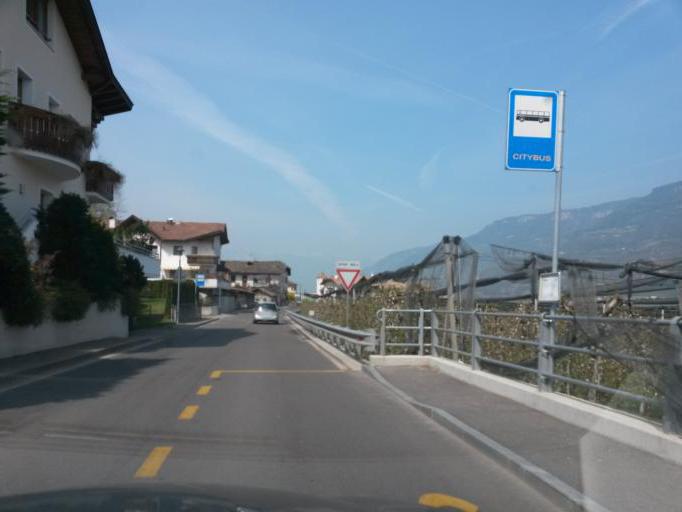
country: IT
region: Trentino-Alto Adige
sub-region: Bolzano
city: San Paolo
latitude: 46.4896
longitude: 11.2607
